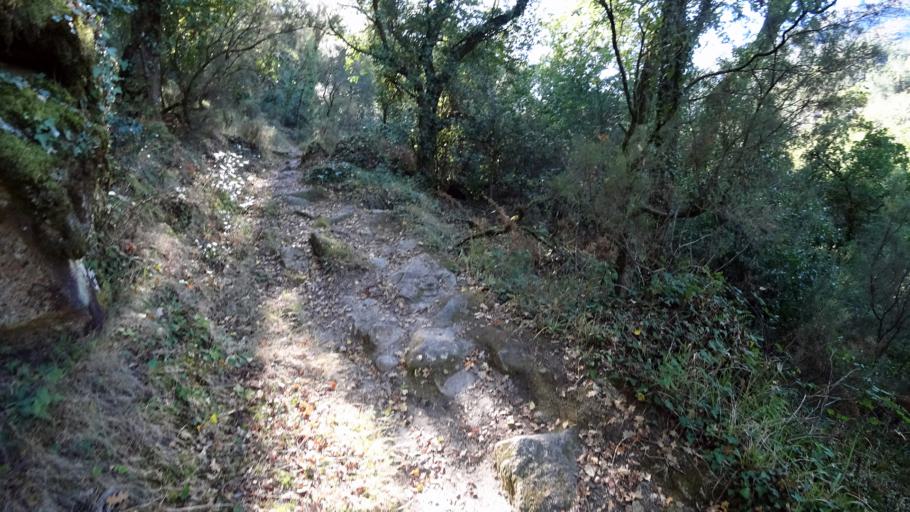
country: ES
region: Galicia
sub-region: Provincia de Ourense
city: Lobios
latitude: 41.7937
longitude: -8.1489
